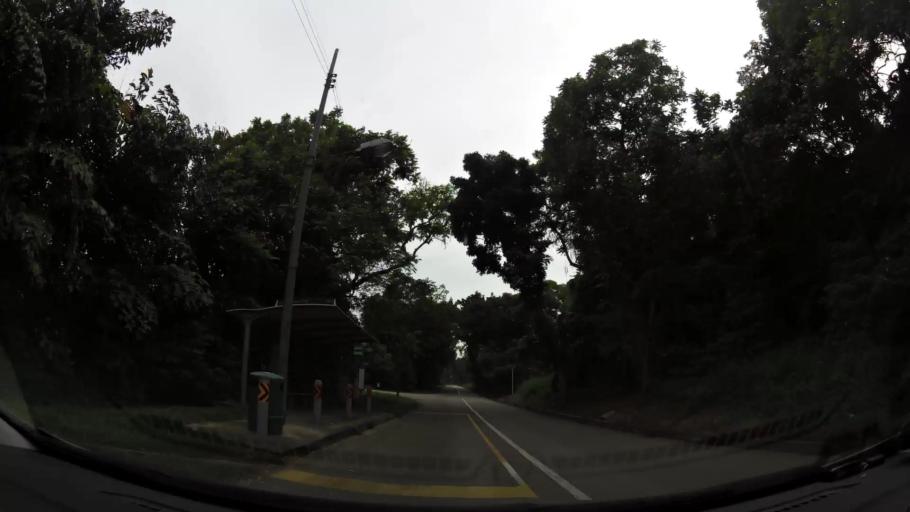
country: MY
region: Johor
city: Johor Bahru
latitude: 1.4424
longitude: 103.7078
